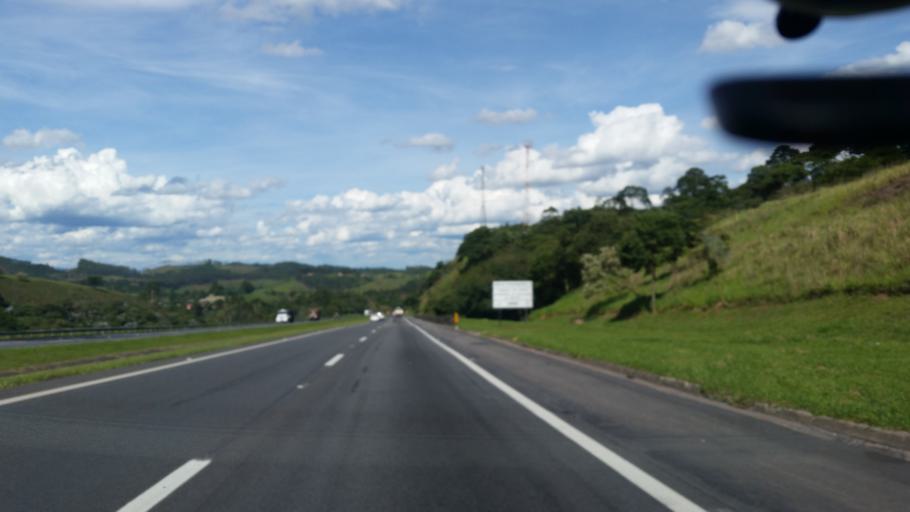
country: BR
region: Sao Paulo
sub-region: Santa Isabel
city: Santa Isabel
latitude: -23.1664
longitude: -46.2367
